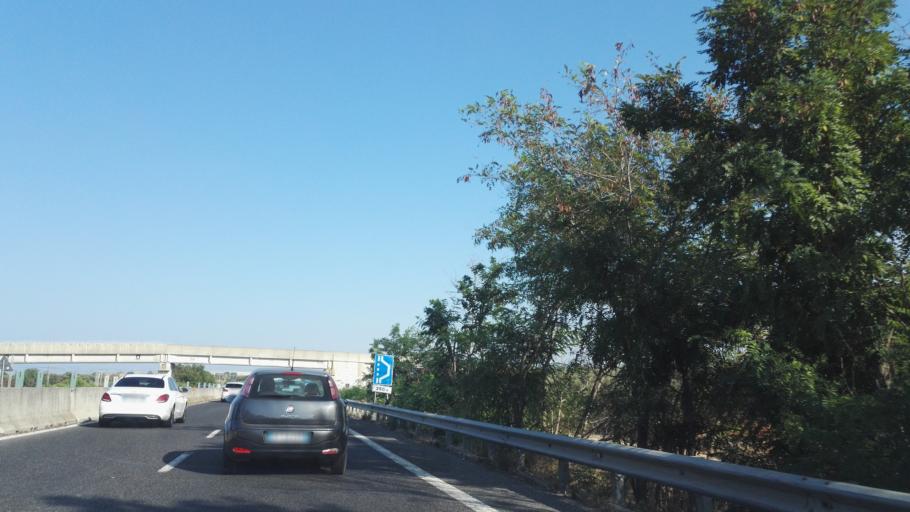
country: IT
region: Apulia
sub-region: Provincia di Bari
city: Mola di Bari
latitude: 41.0475
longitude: 17.1015
